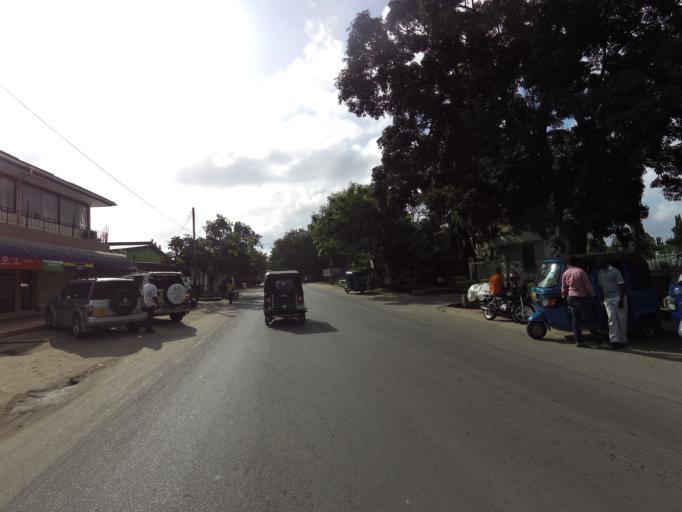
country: TZ
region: Dar es Salaam
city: Magomeni
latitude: -6.7708
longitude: 39.2306
